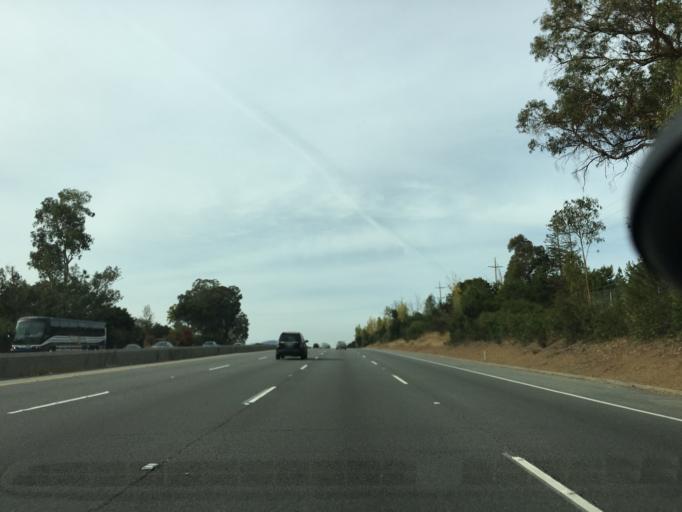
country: US
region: California
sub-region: San Mateo County
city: Emerald Lake Hills
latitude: 37.4489
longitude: -122.2765
